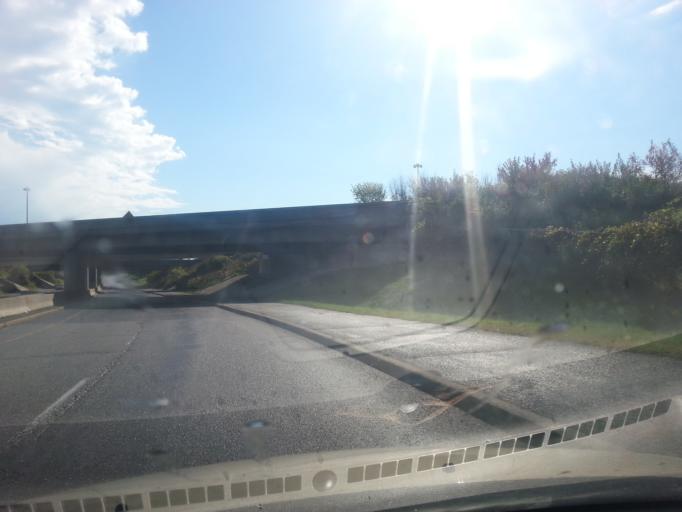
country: CA
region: Ontario
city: Bells Corners
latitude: 45.3447
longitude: -75.8150
